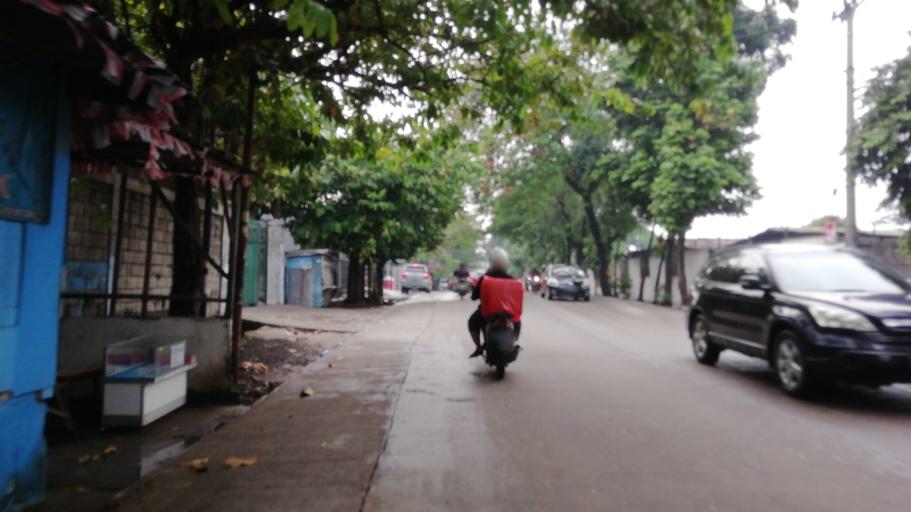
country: ID
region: West Java
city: Bogor
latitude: -6.5554
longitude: 106.8107
